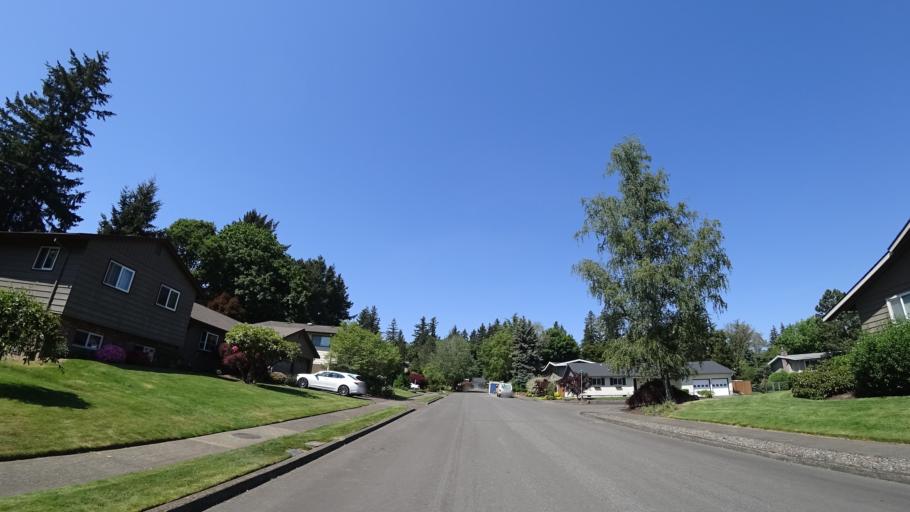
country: US
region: Oregon
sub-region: Washington County
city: Cedar Hills
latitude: 45.4988
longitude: -122.7979
